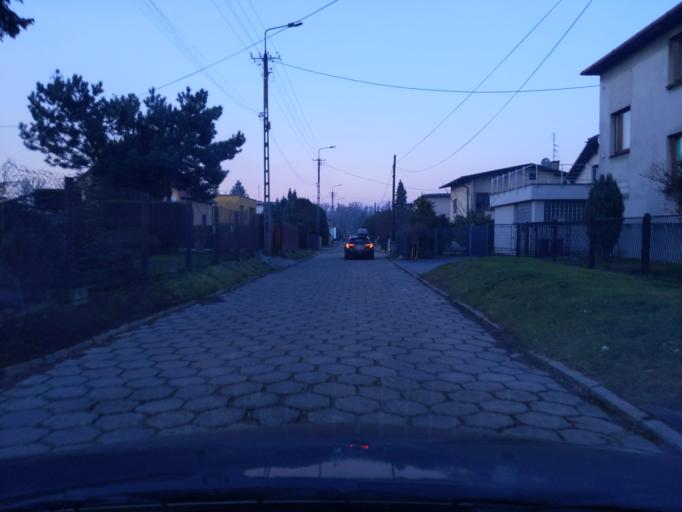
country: PL
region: Silesian Voivodeship
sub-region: Powiat pszczynski
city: Pszczyna
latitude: 49.9687
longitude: 18.9358
